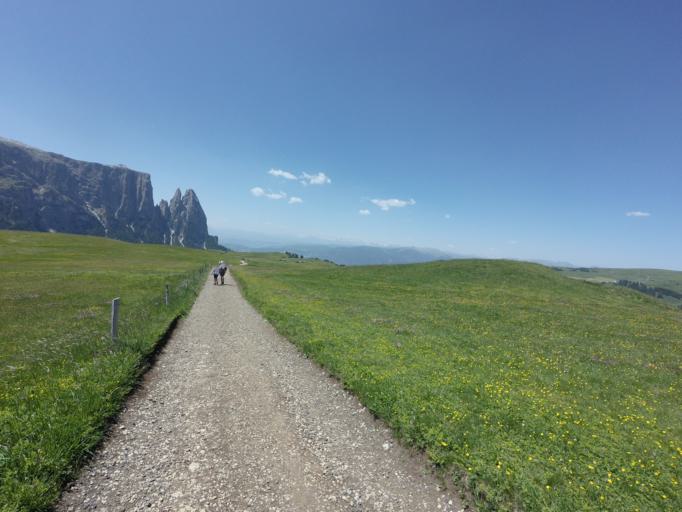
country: IT
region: Trentino-Alto Adige
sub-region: Bolzano
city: Siusi
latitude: 46.5255
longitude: 11.6168
